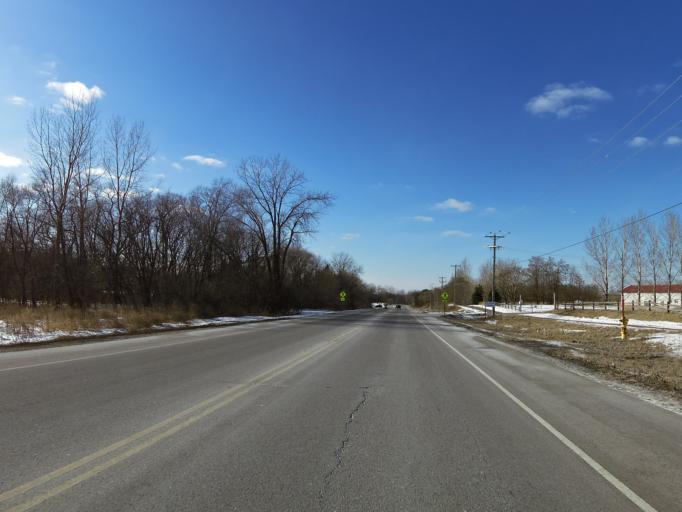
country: US
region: Minnesota
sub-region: Ramsey County
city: Maplewood
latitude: 44.9296
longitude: -92.9882
